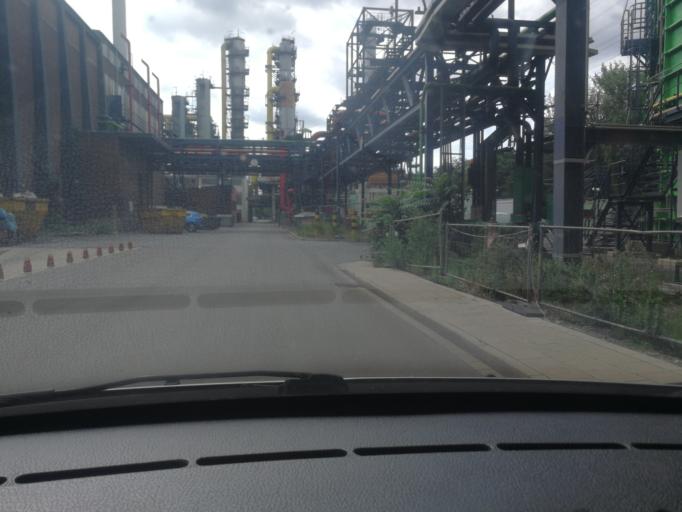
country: DE
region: North Rhine-Westphalia
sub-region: Regierungsbezirk Dusseldorf
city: Hochfeld
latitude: 51.3703
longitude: 6.7050
